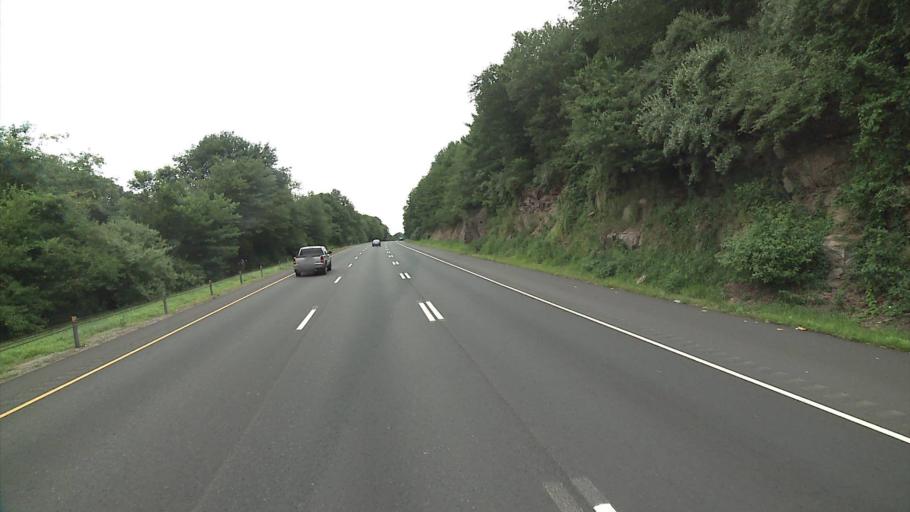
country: US
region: Connecticut
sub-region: Fairfield County
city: Shelton
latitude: 41.2843
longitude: -73.1107
